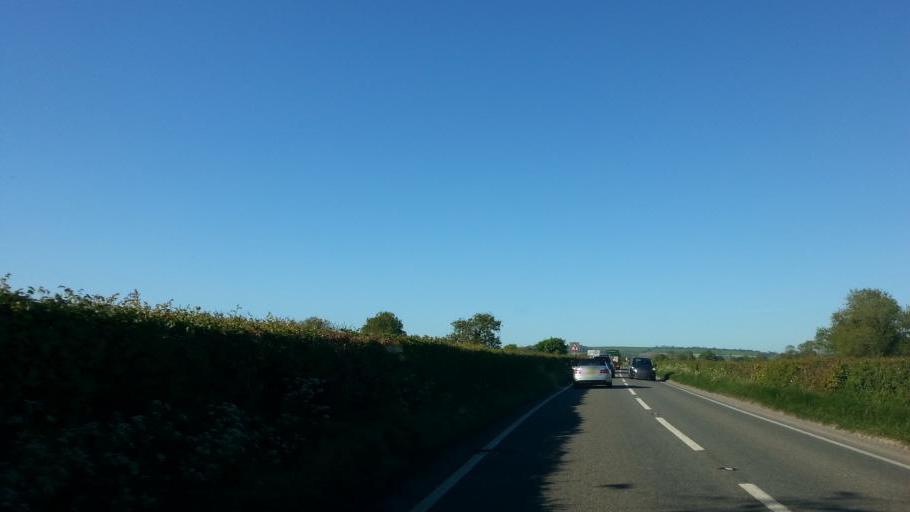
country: GB
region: England
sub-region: Somerset
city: Castle Cary
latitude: 51.1163
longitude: -2.5182
